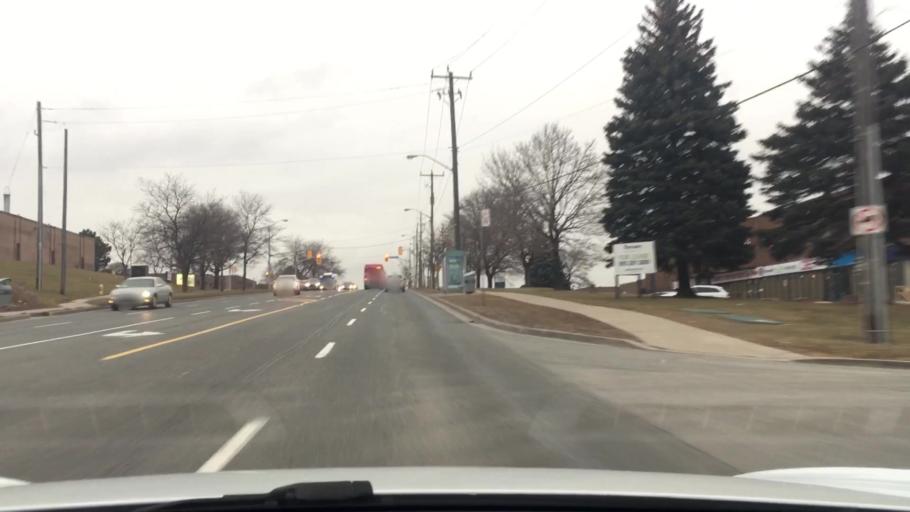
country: CA
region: Ontario
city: Scarborough
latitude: 43.7950
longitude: -79.2610
